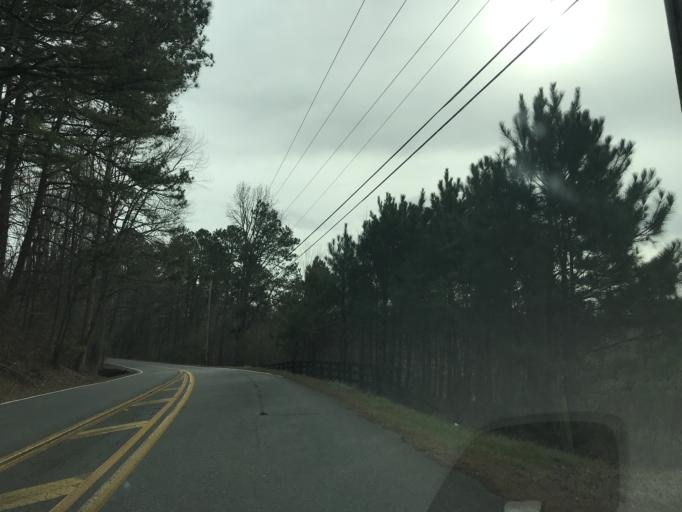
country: US
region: Georgia
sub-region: Cherokee County
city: Canton
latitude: 34.2032
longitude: -84.3923
